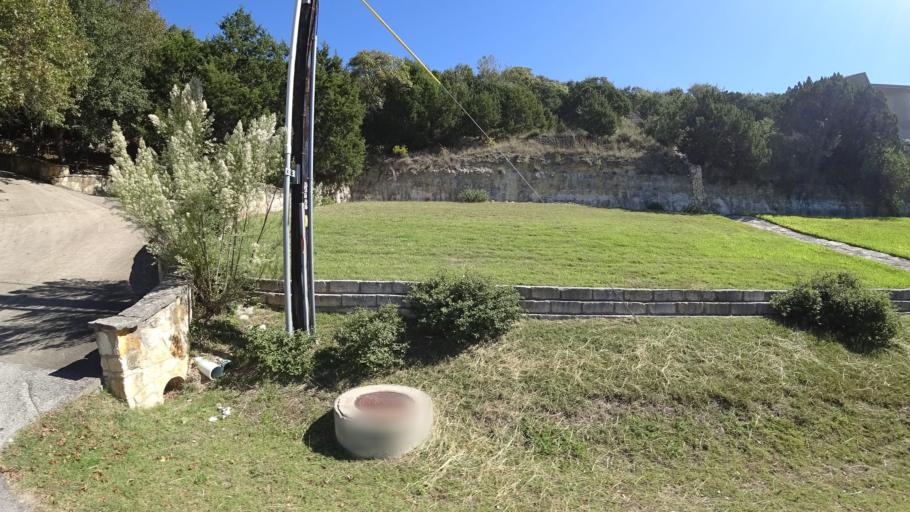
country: US
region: Texas
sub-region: Travis County
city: West Lake Hills
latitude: 30.3122
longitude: -97.8050
